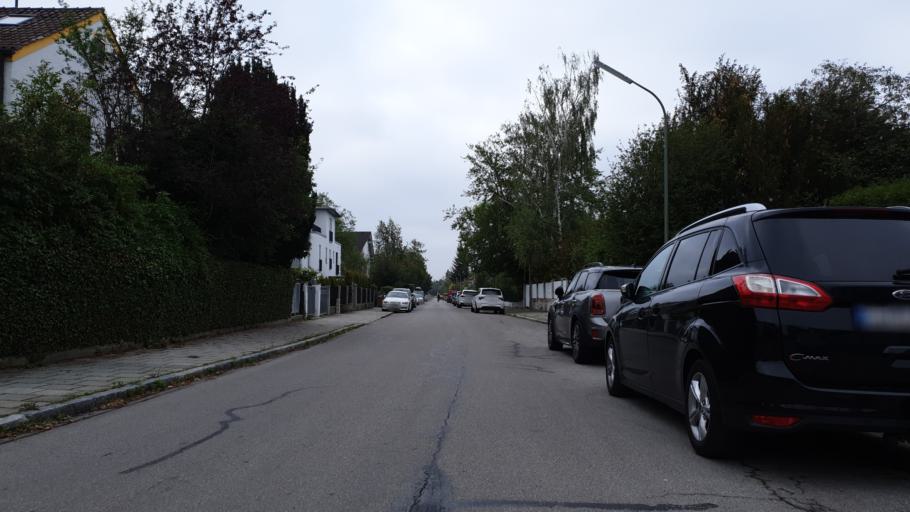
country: DE
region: Bavaria
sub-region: Upper Bavaria
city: Pasing
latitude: 48.1706
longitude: 11.4746
